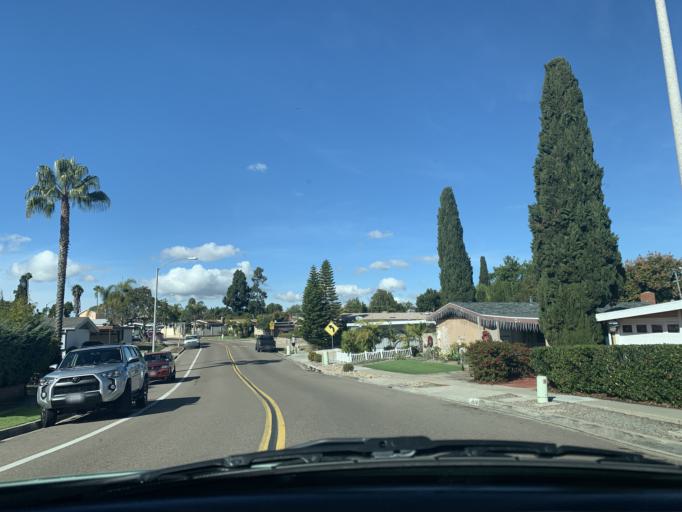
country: US
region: California
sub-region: San Diego County
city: San Diego
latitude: 32.8038
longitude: -117.1351
